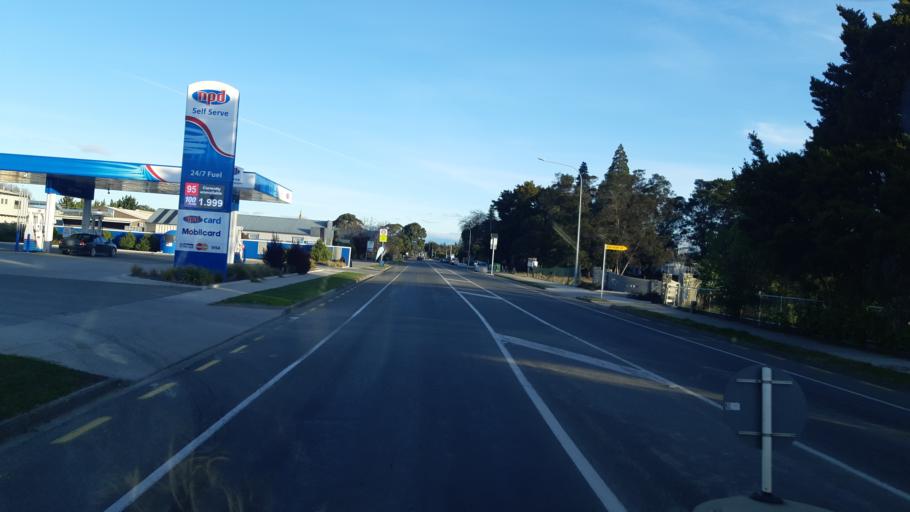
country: NZ
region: Tasman
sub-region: Tasman District
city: Motueka
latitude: -41.1299
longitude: 173.0101
